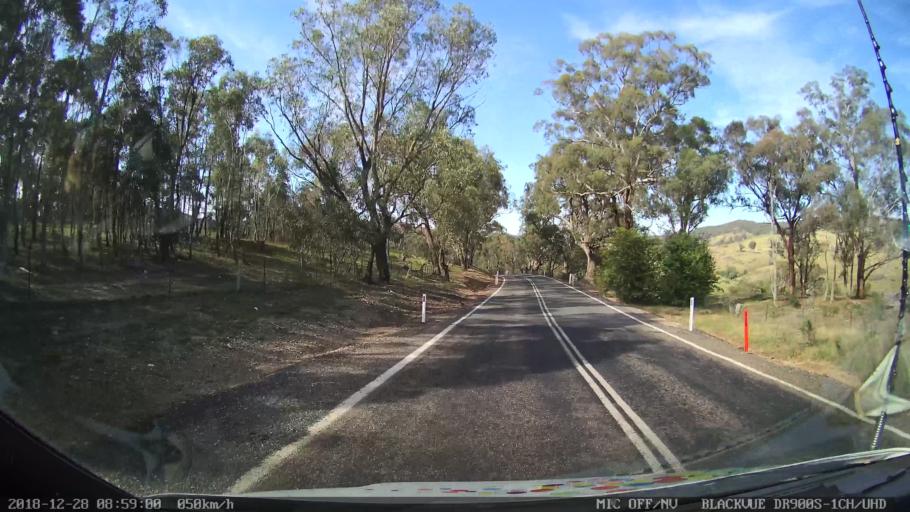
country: AU
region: New South Wales
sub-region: Upper Lachlan Shire
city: Crookwell
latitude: -34.1311
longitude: 149.3329
